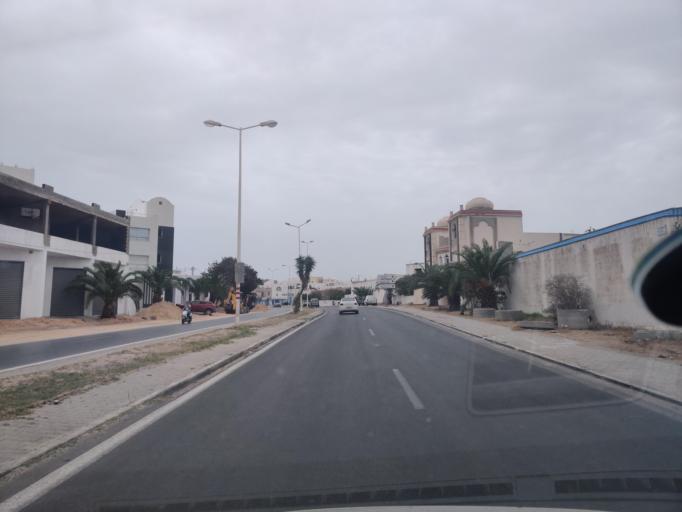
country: TN
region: Nabul
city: Al Hammamat
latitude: 36.4092
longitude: 10.6142
